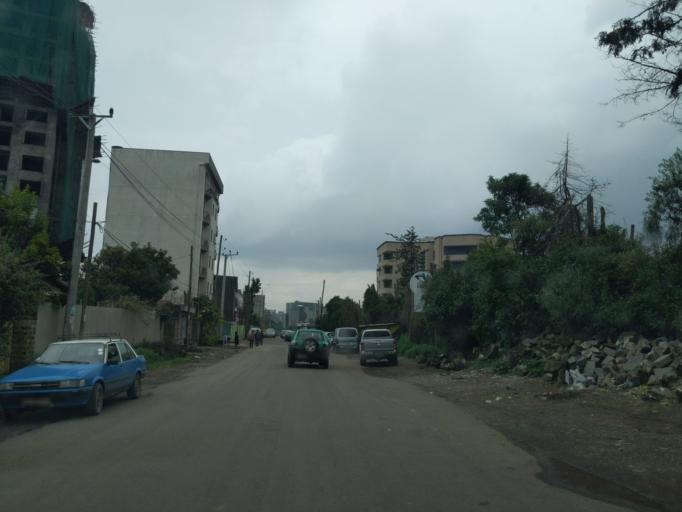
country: ET
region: Adis Abeba
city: Addis Ababa
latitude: 8.9985
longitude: 38.7685
